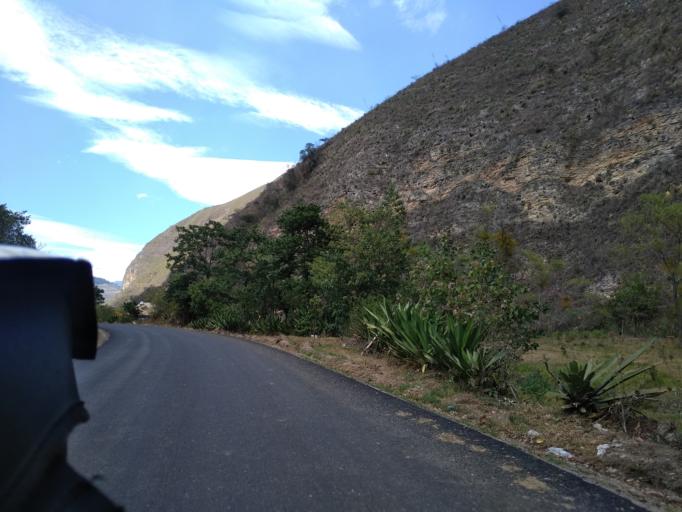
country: PE
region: Amazonas
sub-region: Provincia de Chachapoyas
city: Duraznopampa
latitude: -6.5750
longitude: -77.8272
